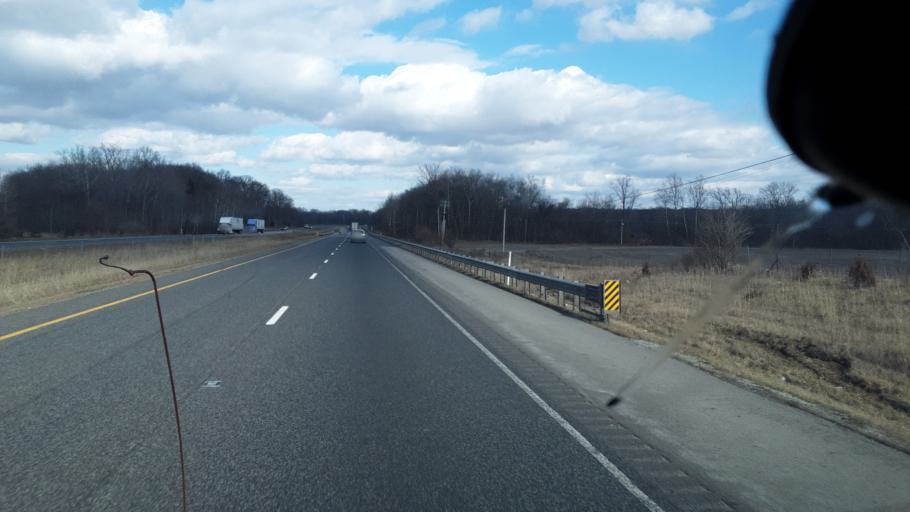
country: US
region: Indiana
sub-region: Henry County
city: Knightstown
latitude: 39.8496
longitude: -85.4908
